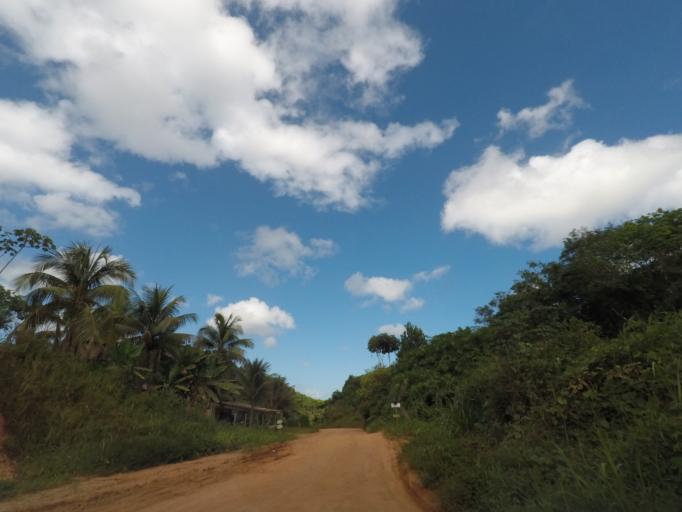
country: BR
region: Bahia
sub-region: Itacare
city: Itacare
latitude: -14.2162
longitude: -39.0631
